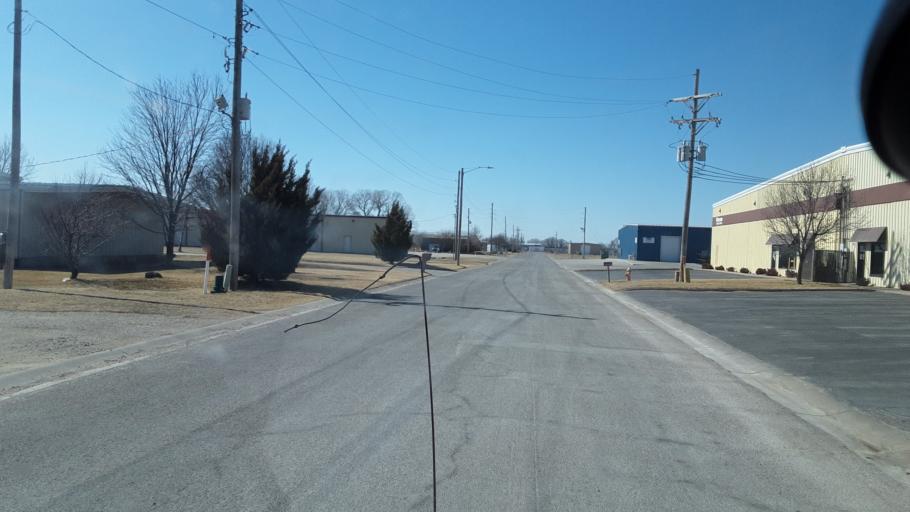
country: US
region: Kansas
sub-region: Reno County
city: Hutchinson
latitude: 38.0696
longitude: -97.8787
